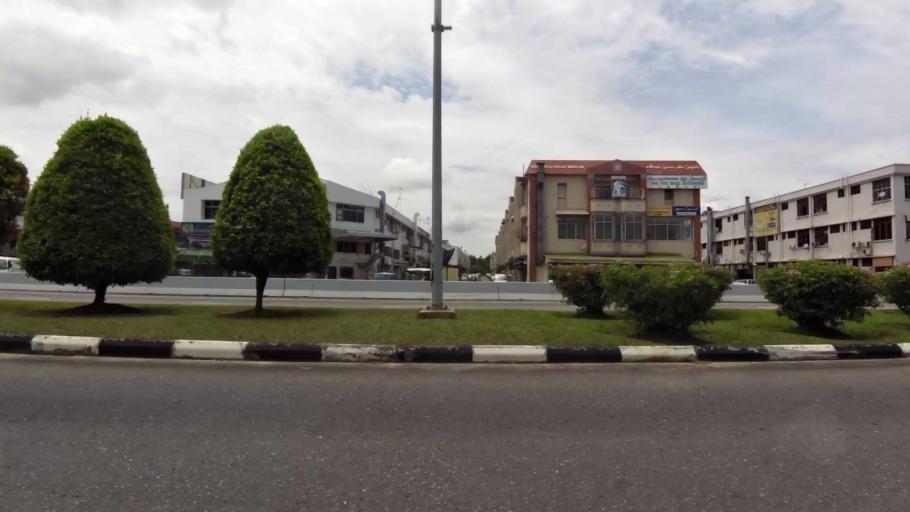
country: BN
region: Brunei and Muara
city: Bandar Seri Begawan
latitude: 4.9092
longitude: 114.9238
